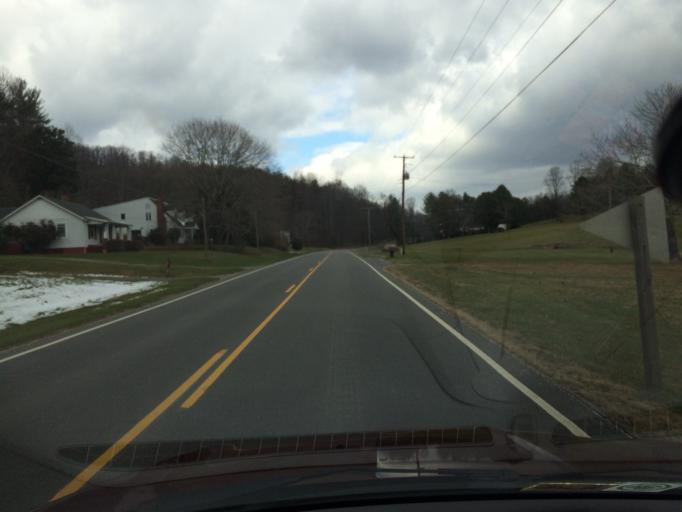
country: US
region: Virginia
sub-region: Patrick County
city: Stuart
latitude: 36.7281
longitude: -80.2423
